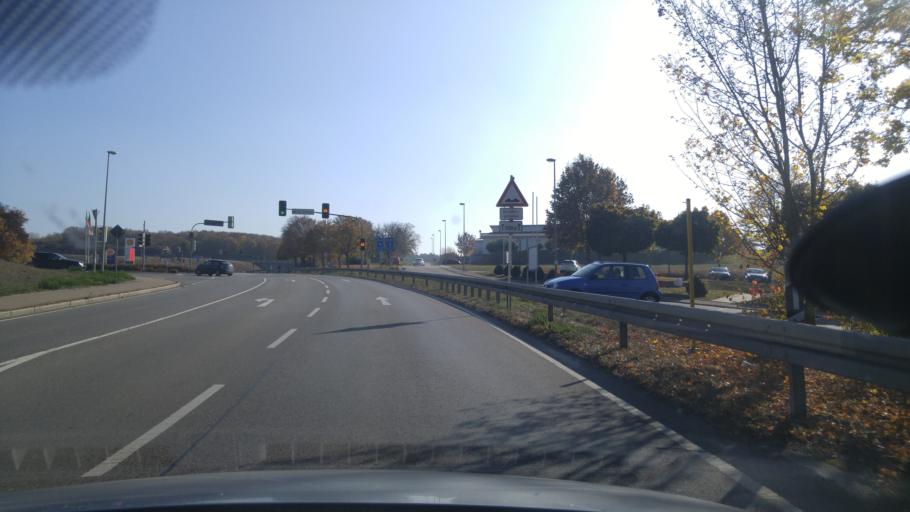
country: DE
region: Baden-Wuerttemberg
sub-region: Karlsruhe Region
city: Empfingen
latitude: 48.3863
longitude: 8.7211
